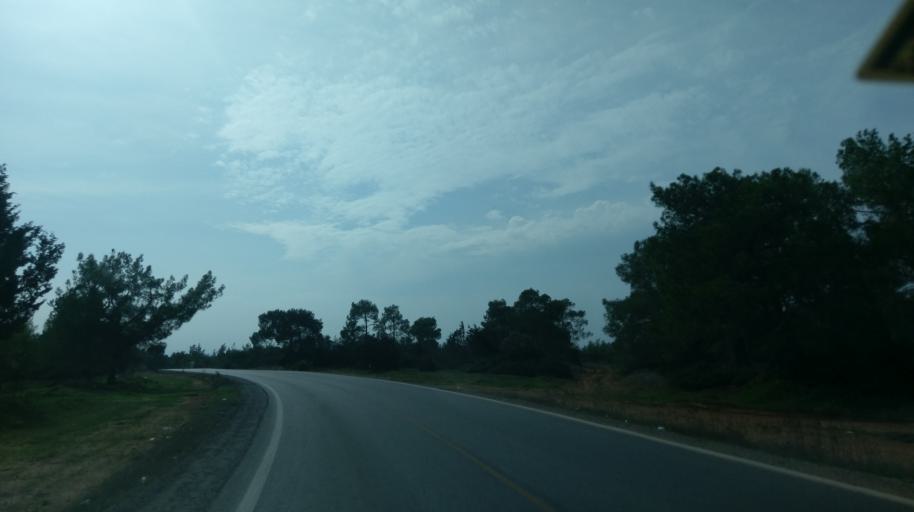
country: CY
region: Lefkosia
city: Morfou
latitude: 35.2894
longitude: 33.0413
